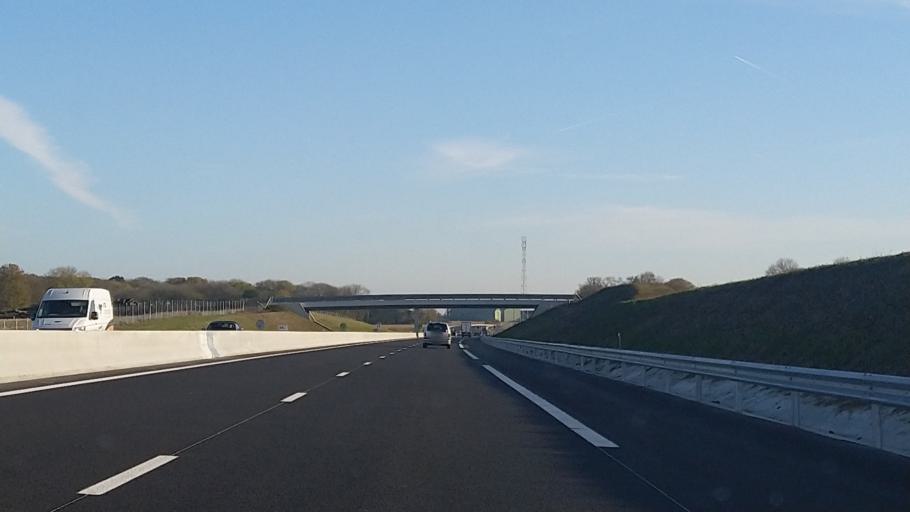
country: FR
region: Ile-de-France
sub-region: Departement du Val-d'Oise
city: Maffliers
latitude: 49.0877
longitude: 2.3135
